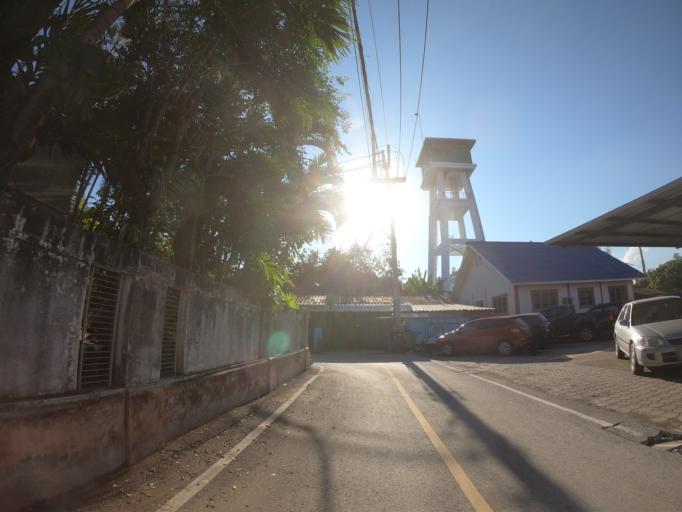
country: TH
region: Chiang Mai
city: San Sai
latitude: 18.8278
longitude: 99.0306
